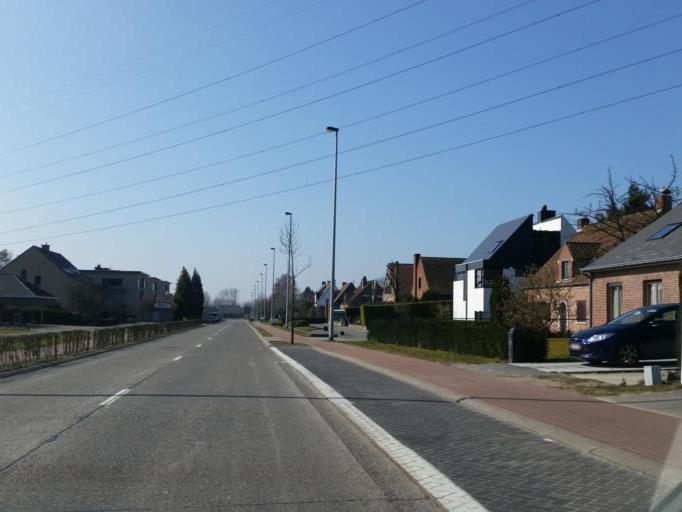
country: BE
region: Flanders
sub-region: Provincie Antwerpen
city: Bornem
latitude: 51.1294
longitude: 4.2521
